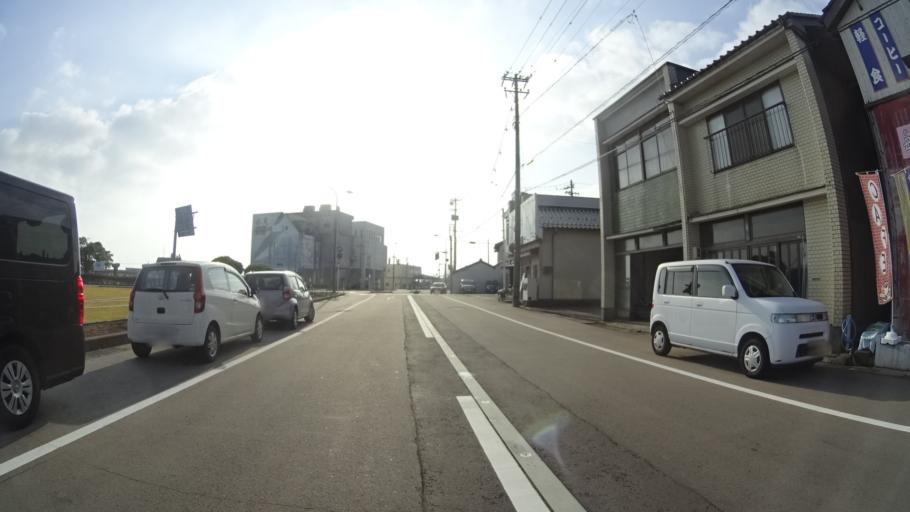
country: JP
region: Toyama
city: Himi
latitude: 36.8607
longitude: 136.9880
